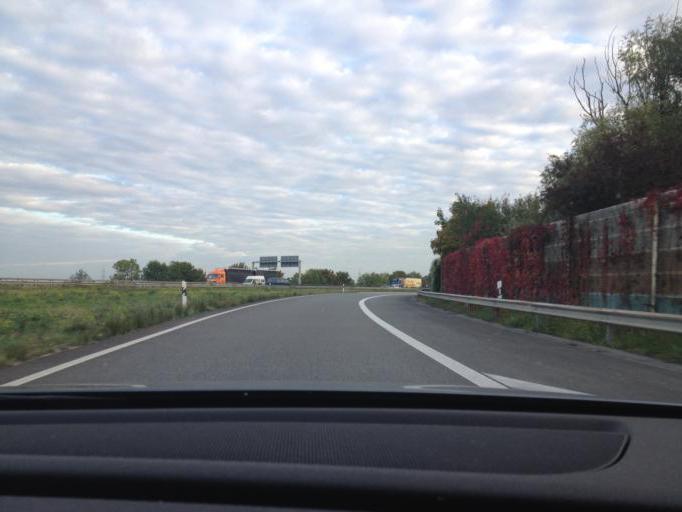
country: DE
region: Rheinland-Pfalz
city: Hessheim
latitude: 49.5518
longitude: 8.3132
